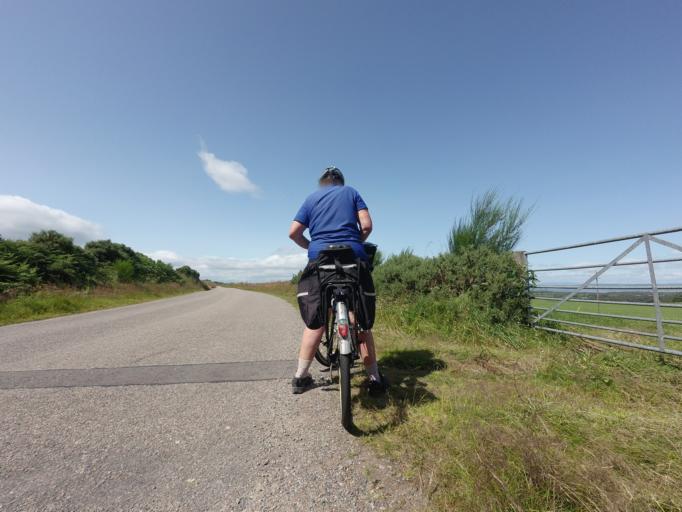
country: GB
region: Scotland
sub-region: Highland
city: Nairn
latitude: 57.5008
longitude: -3.9741
